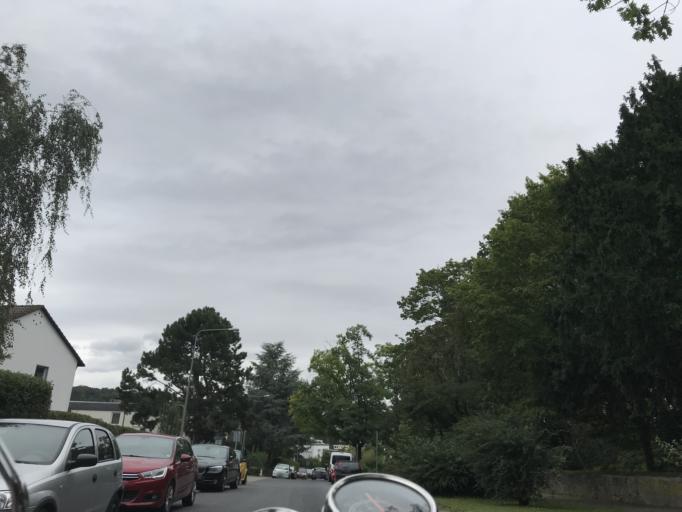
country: DE
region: Hesse
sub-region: Regierungsbezirk Darmstadt
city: Wiesbaden
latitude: 50.0907
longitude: 8.2306
